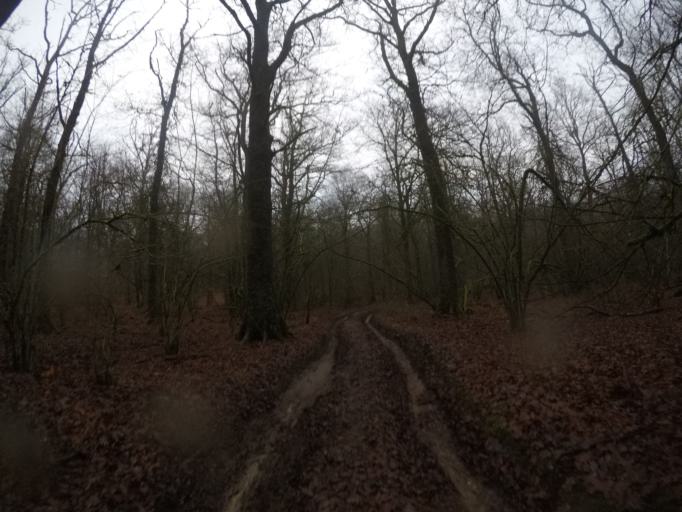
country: BE
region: Wallonia
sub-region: Province du Luxembourg
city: Leglise
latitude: 49.8133
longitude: 5.6035
